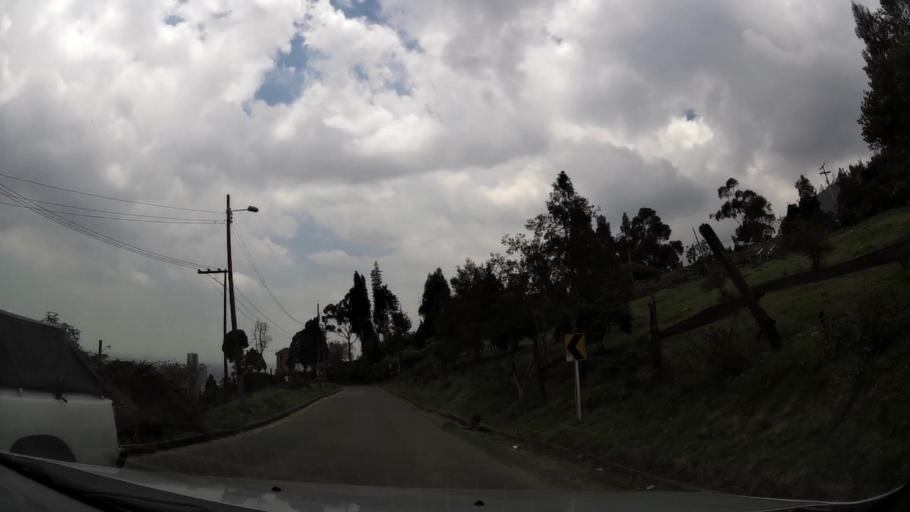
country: CO
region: Bogota D.C.
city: Bogota
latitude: 4.5952
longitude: -74.0656
